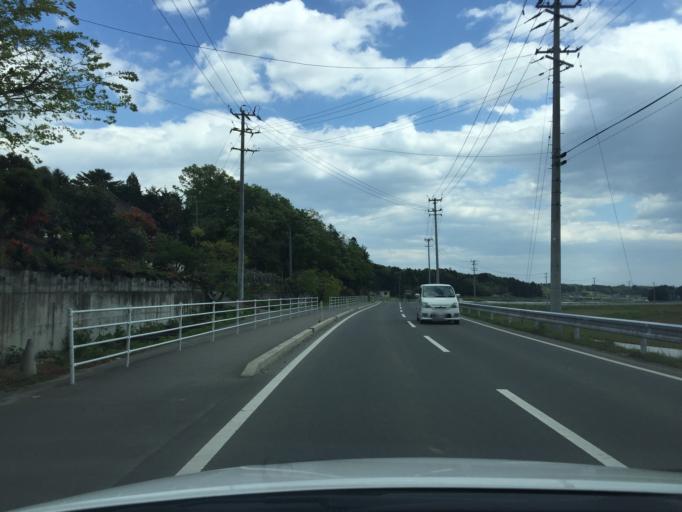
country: JP
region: Miyagi
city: Marumori
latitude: 37.7372
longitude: 140.9220
